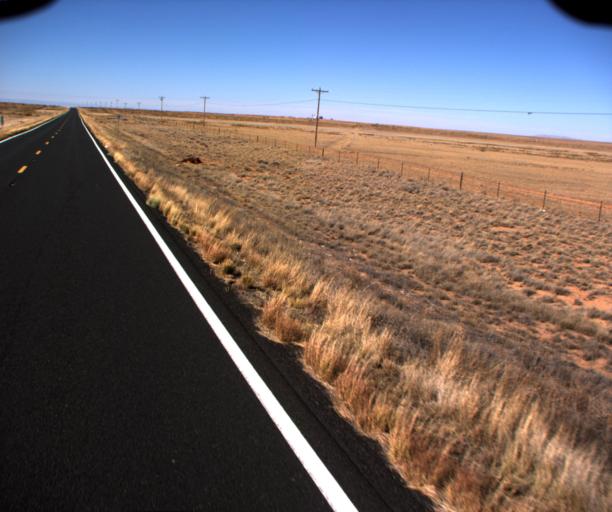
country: US
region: Arizona
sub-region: Coconino County
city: Tuba City
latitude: 36.0004
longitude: -111.0364
